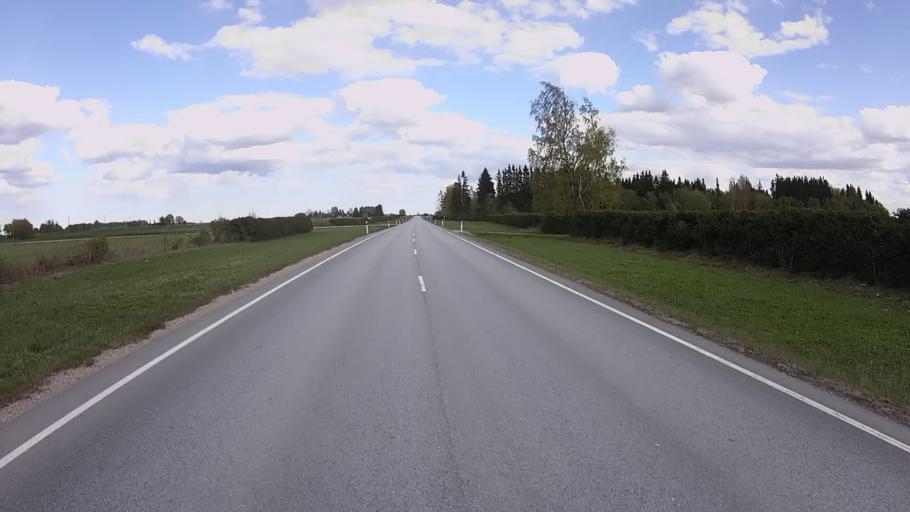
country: EE
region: Jogevamaa
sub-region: Jogeva linn
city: Jogeva
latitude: 58.8256
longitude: 26.6113
